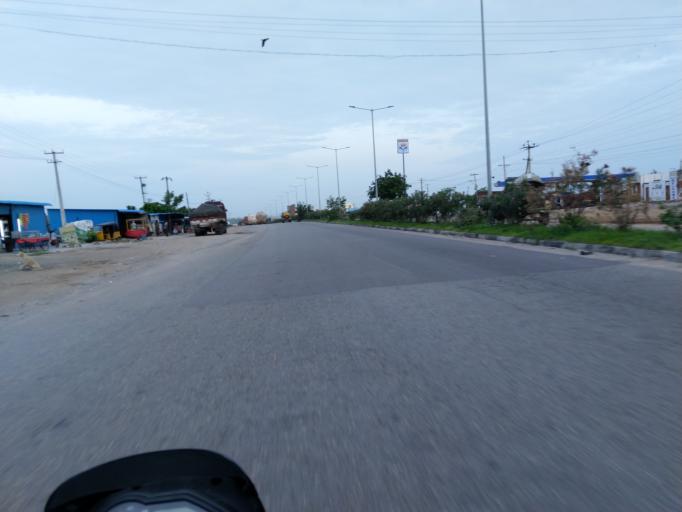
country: IN
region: Telangana
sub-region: Rangareddi
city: Lal Bahadur Nagar
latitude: 17.3172
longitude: 78.6653
